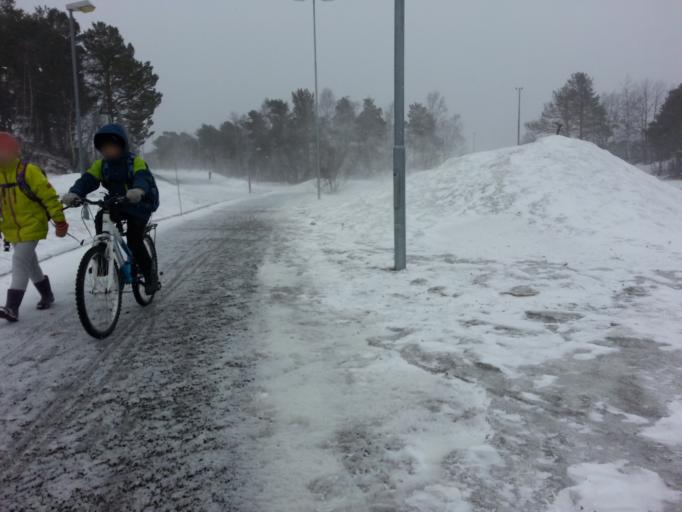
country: NO
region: Sor-Trondelag
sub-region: Oppdal
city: Oppdal
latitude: 62.5965
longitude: 9.6819
